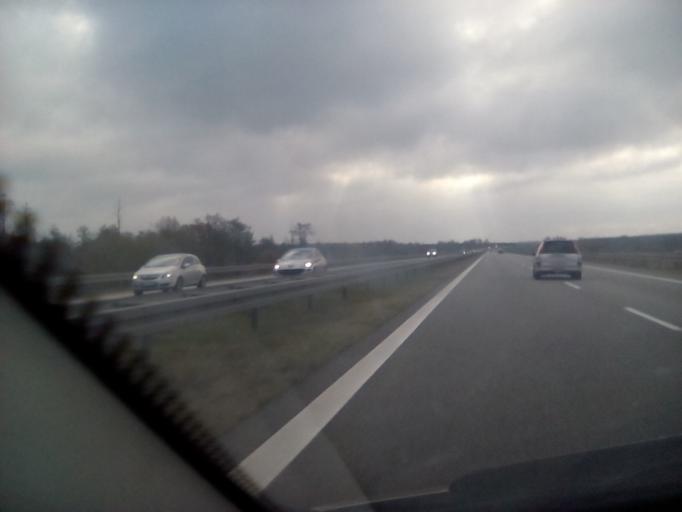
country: PL
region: Masovian Voivodeship
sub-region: Powiat bialobrzeski
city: Promna
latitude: 51.6632
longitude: 20.9583
